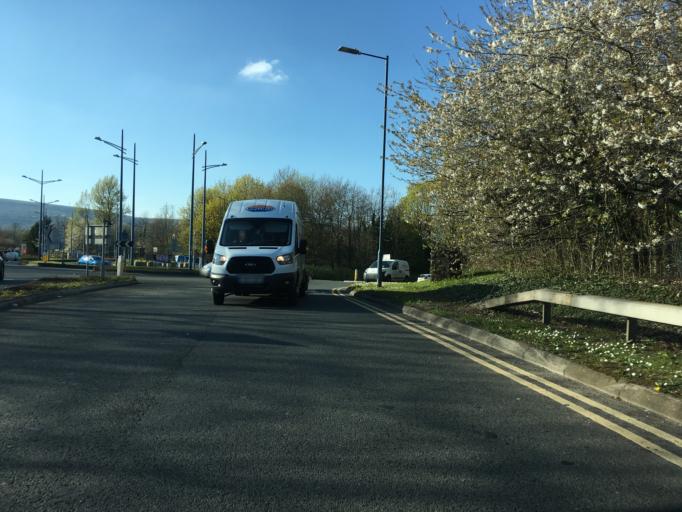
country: GB
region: Wales
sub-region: Torfaen County Borough
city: Cwmbran
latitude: 51.6438
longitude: -3.0225
